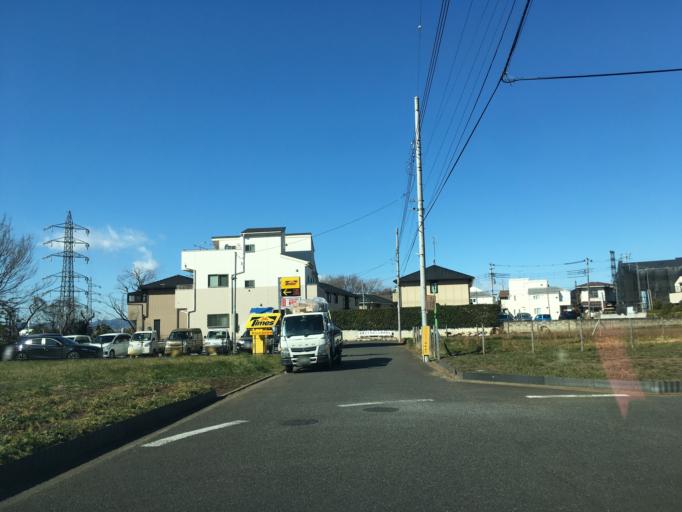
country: JP
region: Tokyo
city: Kokubunji
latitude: 35.6715
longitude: 139.4553
